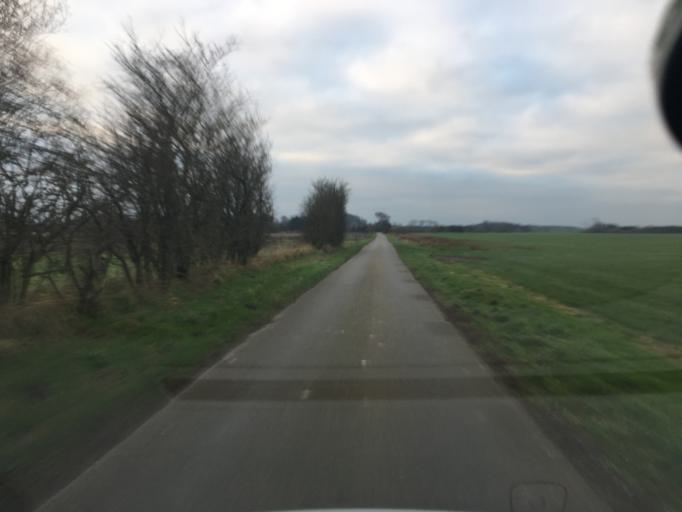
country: DK
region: South Denmark
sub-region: Tonder Kommune
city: Toftlund
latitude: 55.0812
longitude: 9.0866
